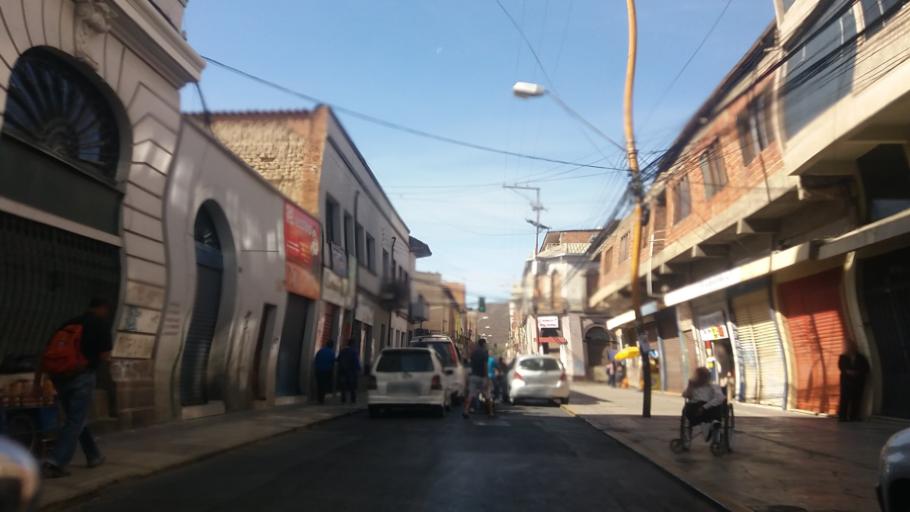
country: BO
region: Cochabamba
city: Cochabamba
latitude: -17.3964
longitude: -66.1565
